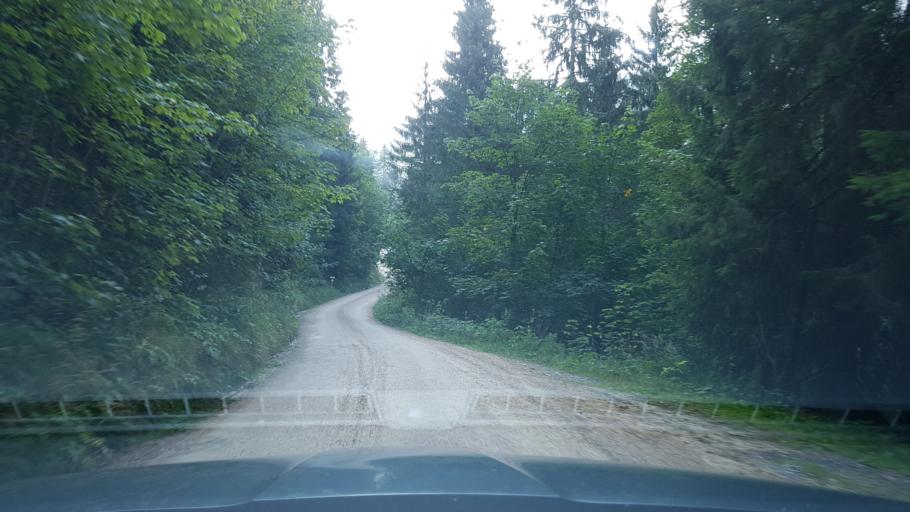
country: AT
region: Salzburg
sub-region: Politischer Bezirk Sankt Johann im Pongau
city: Kleinarl
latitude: 47.2743
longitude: 13.2483
